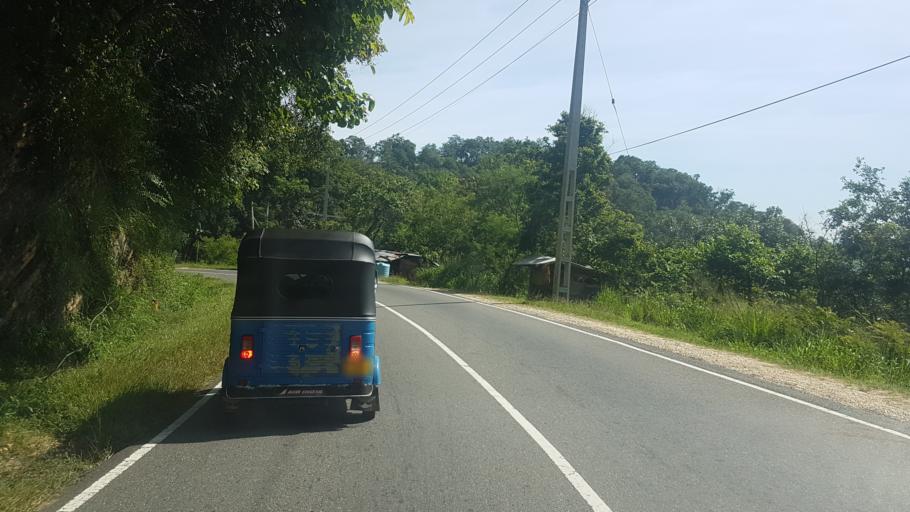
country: LK
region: Uva
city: Haputale
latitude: 6.8031
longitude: 81.0891
